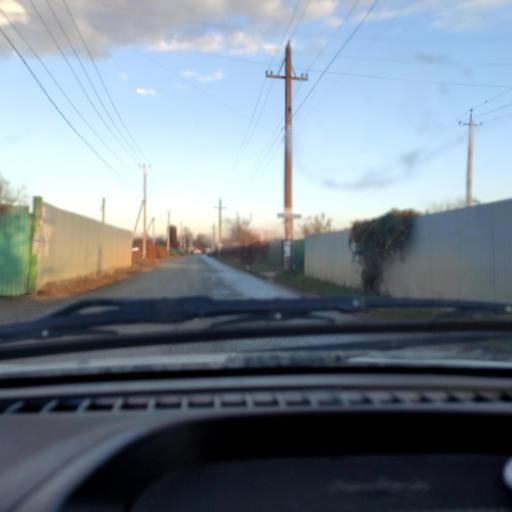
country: RU
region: Samara
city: Povolzhskiy
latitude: 53.4662
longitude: 49.6506
